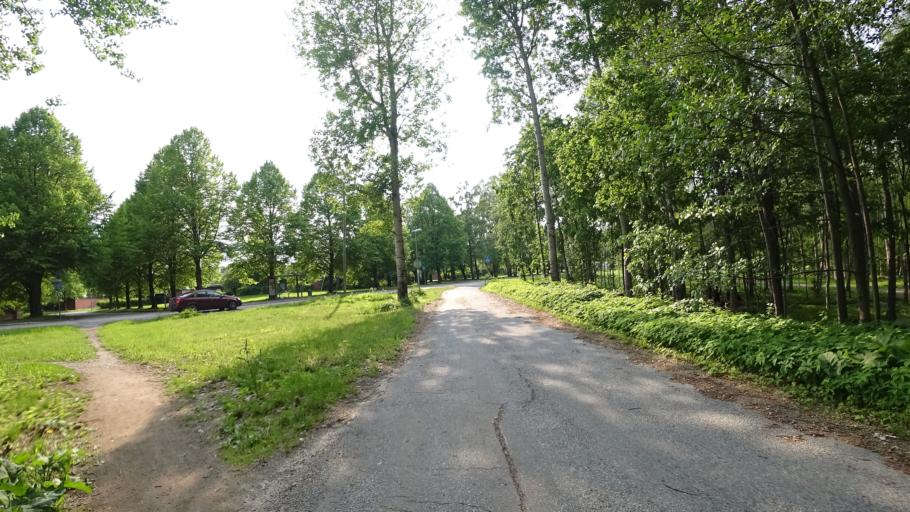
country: FI
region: Pirkanmaa
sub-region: Tampere
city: Pirkkala
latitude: 61.5022
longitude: 23.6645
